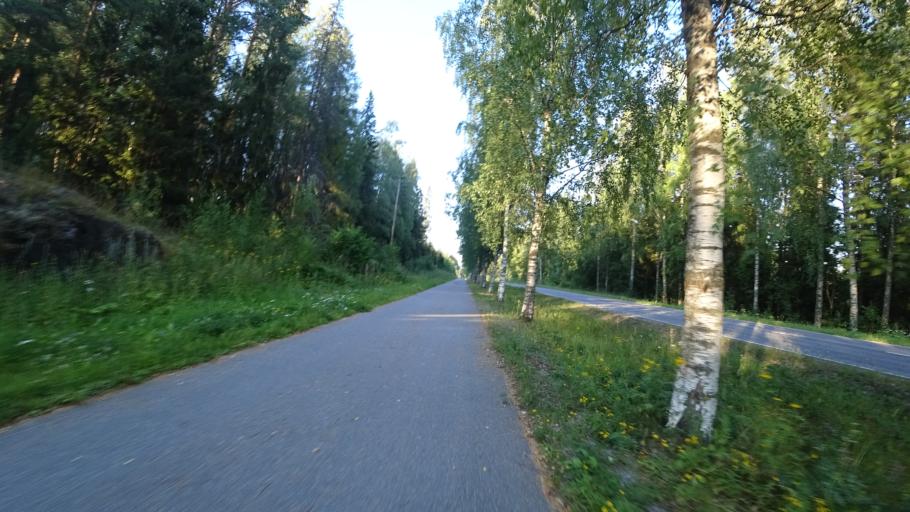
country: FI
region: Pirkanmaa
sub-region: Tampere
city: Nokia
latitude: 61.4708
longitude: 23.4602
